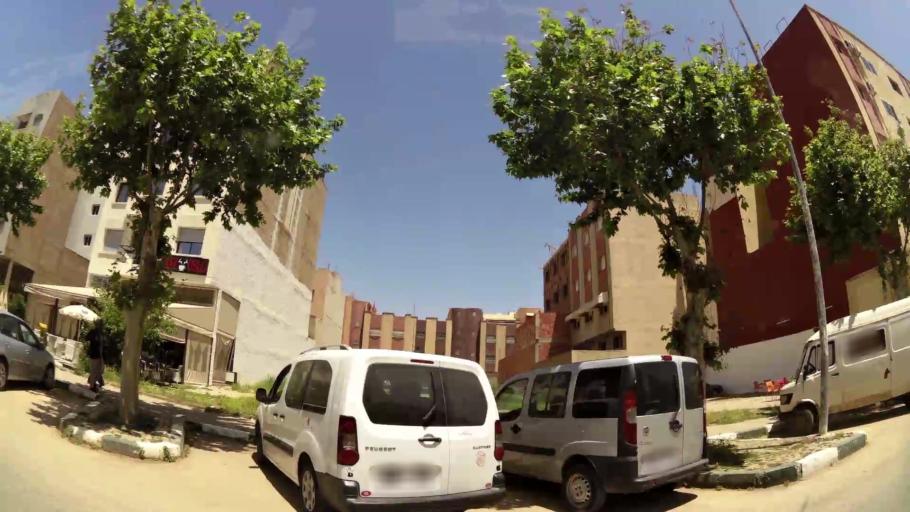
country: MA
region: Rabat-Sale-Zemmour-Zaer
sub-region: Khemisset
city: Khemisset
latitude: 33.8266
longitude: -6.0810
